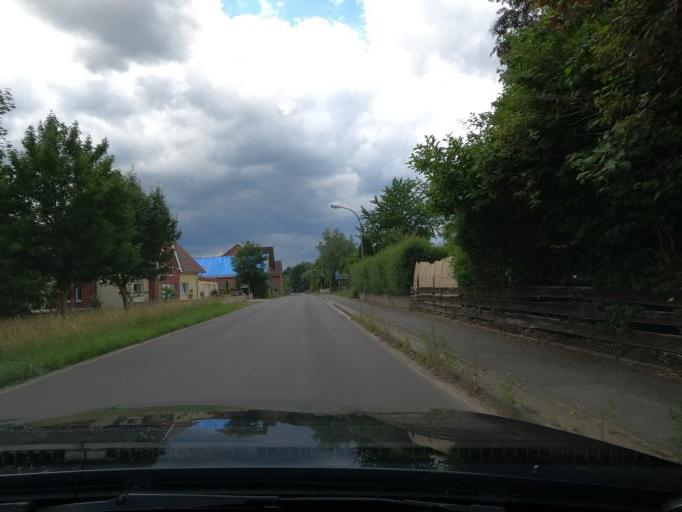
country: DE
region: Lower Saxony
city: Baddeckenstedt
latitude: 52.0960
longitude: 10.2282
